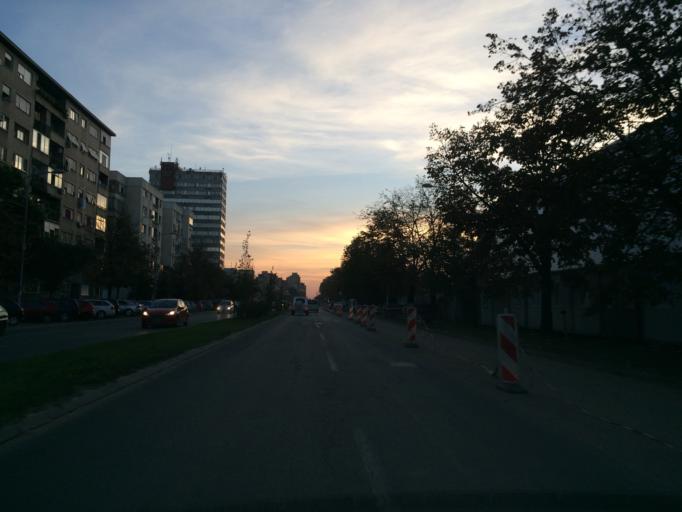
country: RS
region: Autonomna Pokrajina Vojvodina
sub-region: Juznobacki Okrug
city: Novi Sad
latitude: 45.2445
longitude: 19.8448
